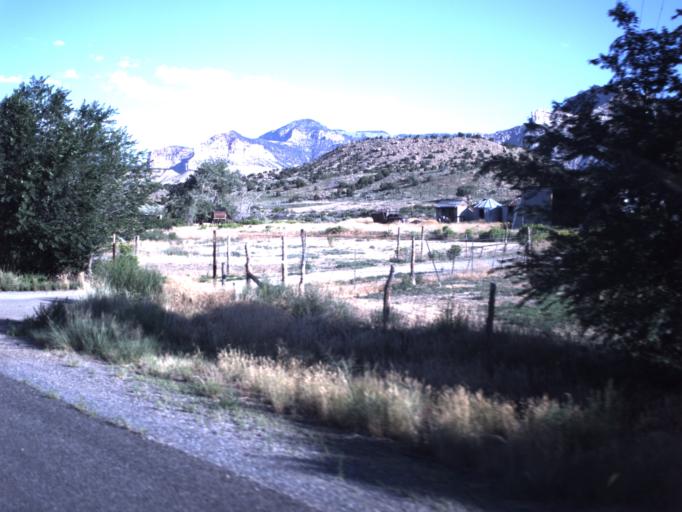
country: US
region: Utah
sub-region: Emery County
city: Huntington
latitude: 39.3530
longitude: -111.0123
